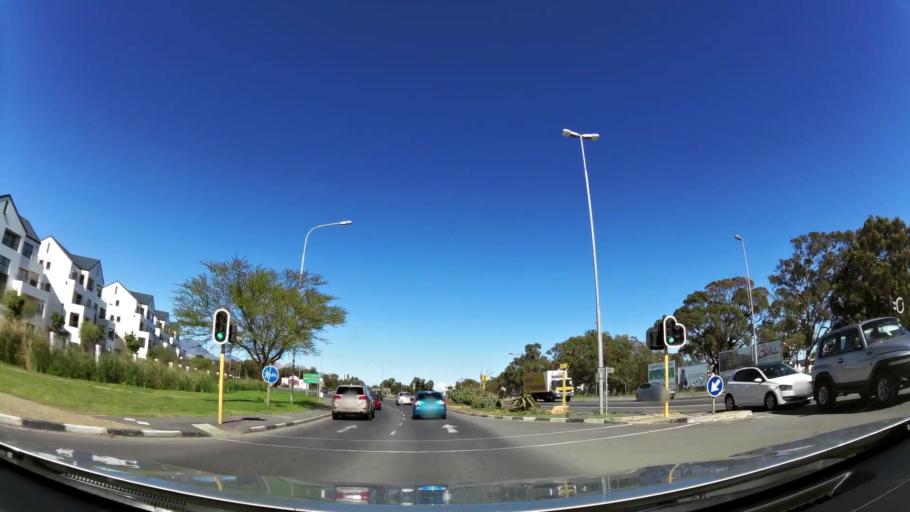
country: ZA
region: Western Cape
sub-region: Cape Winelands District Municipality
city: Stellenbosch
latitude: -34.0902
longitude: 18.8193
